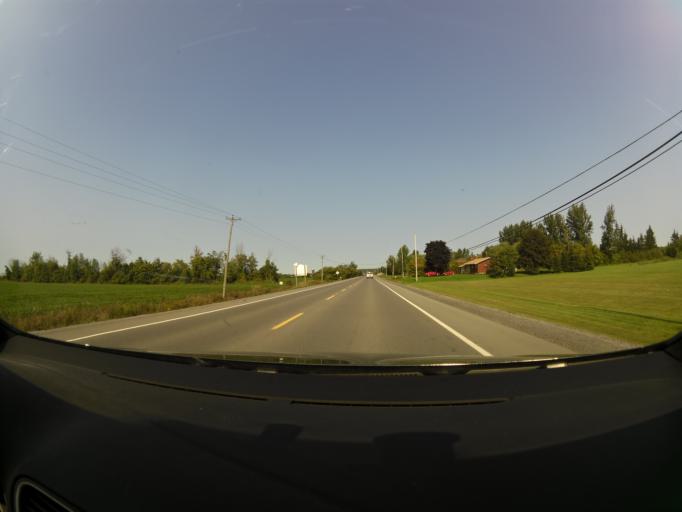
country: CA
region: Ontario
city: Bells Corners
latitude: 45.3254
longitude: -76.0118
